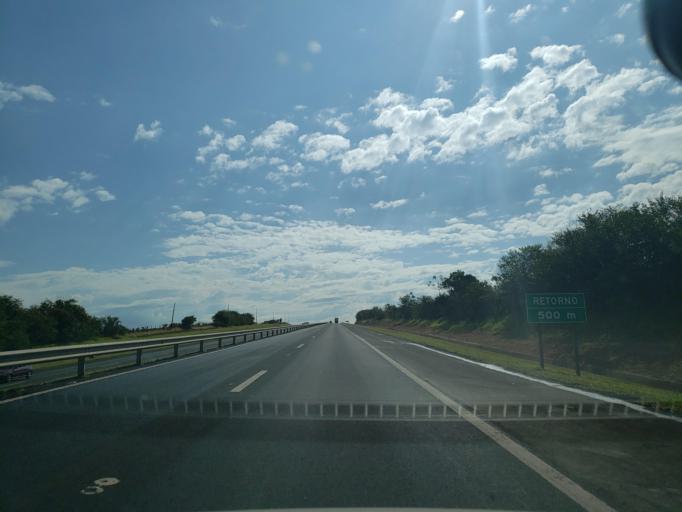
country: BR
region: Sao Paulo
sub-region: Pirajui
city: Pirajui
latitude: -22.0248
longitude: -49.4084
